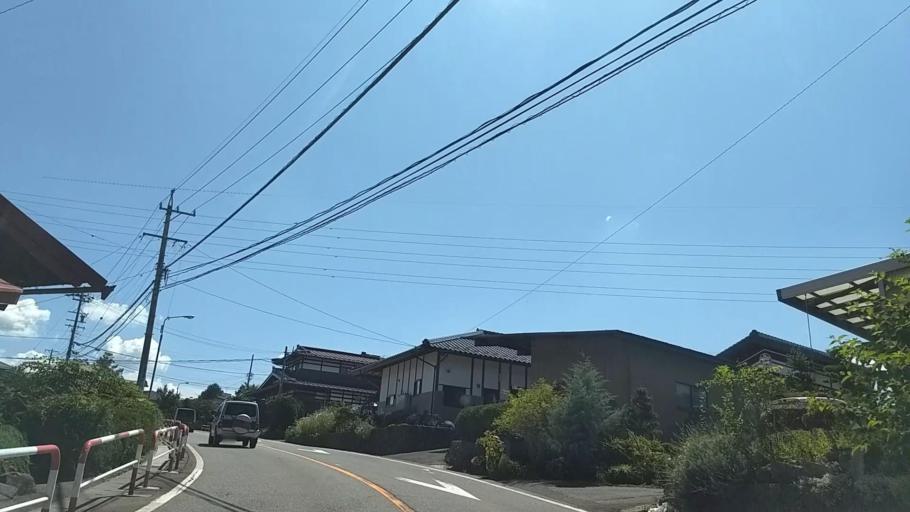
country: JP
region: Nagano
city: Chino
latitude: 36.0374
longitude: 138.2238
